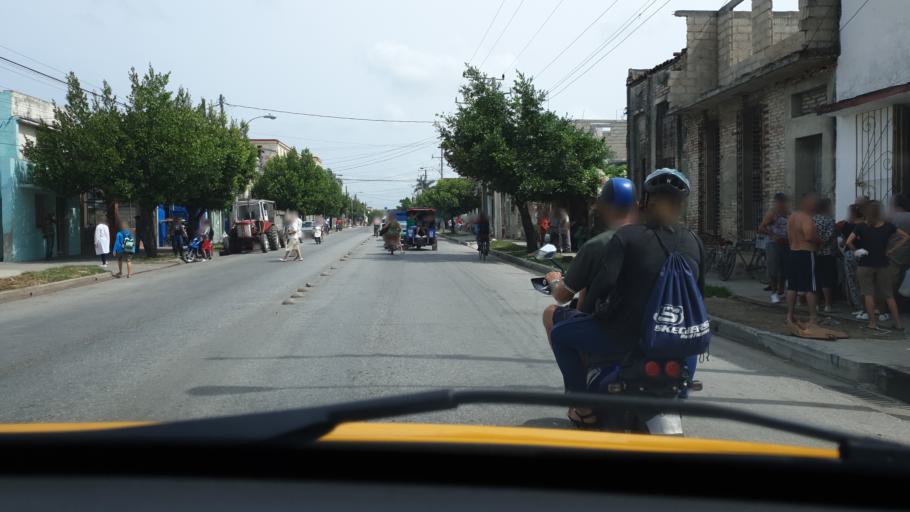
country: CU
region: Villa Clara
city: Santa Clara
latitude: 22.3979
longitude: -79.9632
